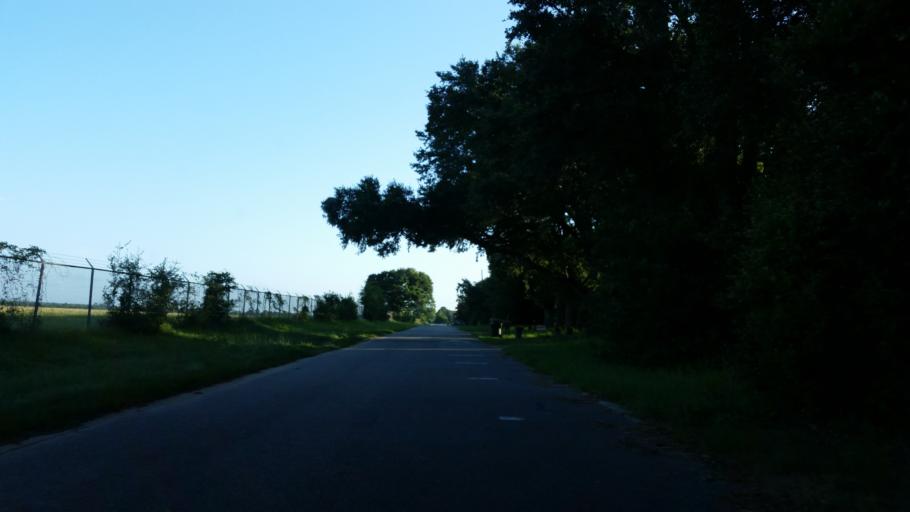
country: US
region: Florida
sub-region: Escambia County
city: Bellview
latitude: 30.4643
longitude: -87.3326
